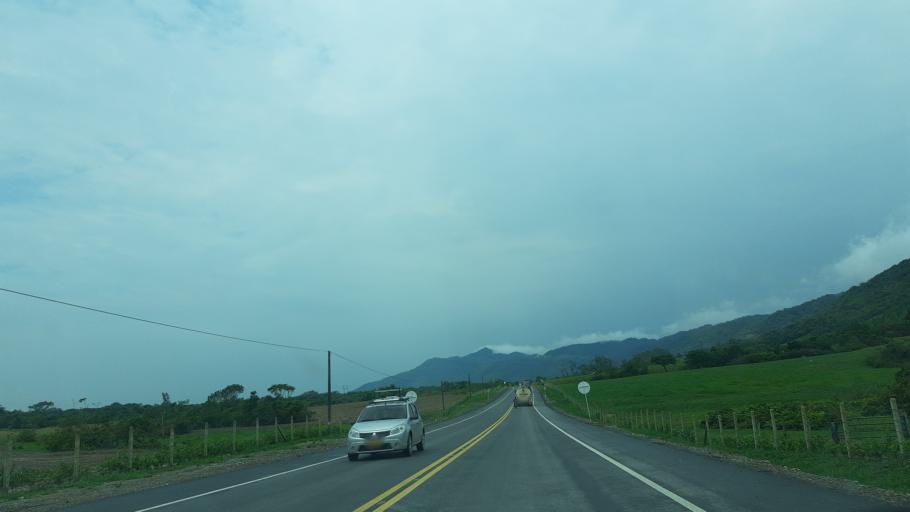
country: CO
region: Casanare
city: Sabanalarga
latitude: 4.8001
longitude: -72.9837
